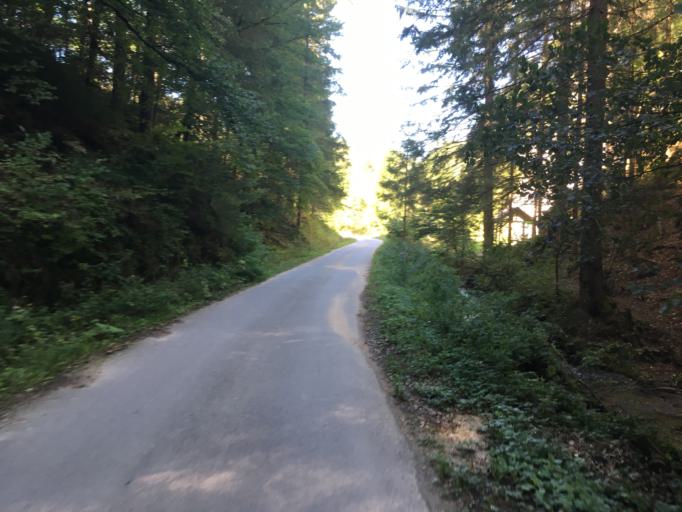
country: SK
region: Trenciansky
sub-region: Okres Povazska Bystrica
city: Povazska Bystrica
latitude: 49.0040
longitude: 18.4683
